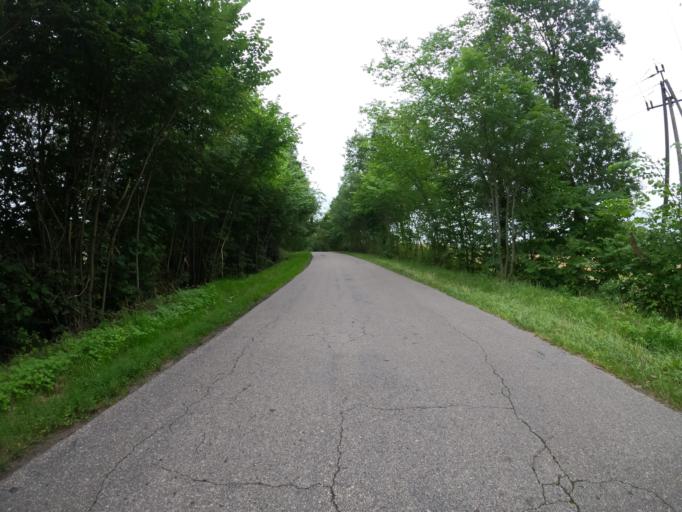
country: PL
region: West Pomeranian Voivodeship
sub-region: Powiat szczecinecki
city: Grzmiaca
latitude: 53.9386
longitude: 16.4577
